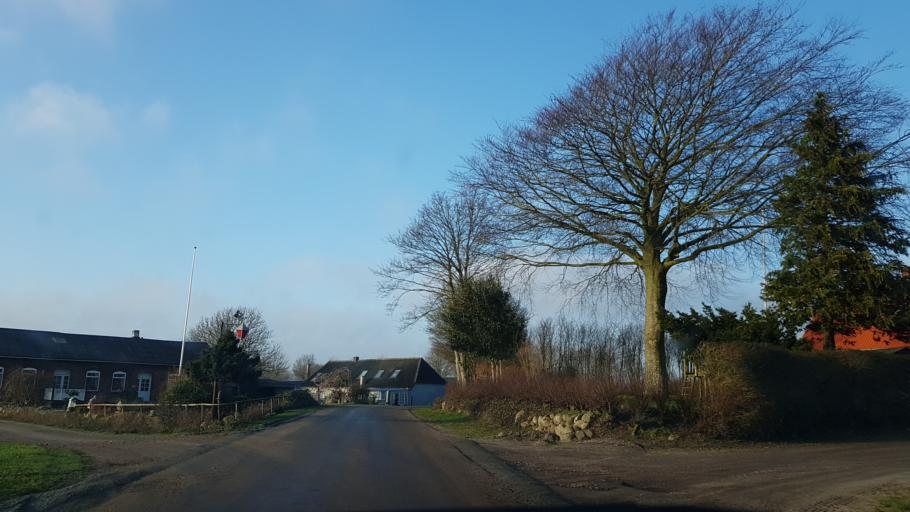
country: DK
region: South Denmark
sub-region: Aabenraa Kommune
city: Rodekro
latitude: 55.1552
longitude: 9.3122
